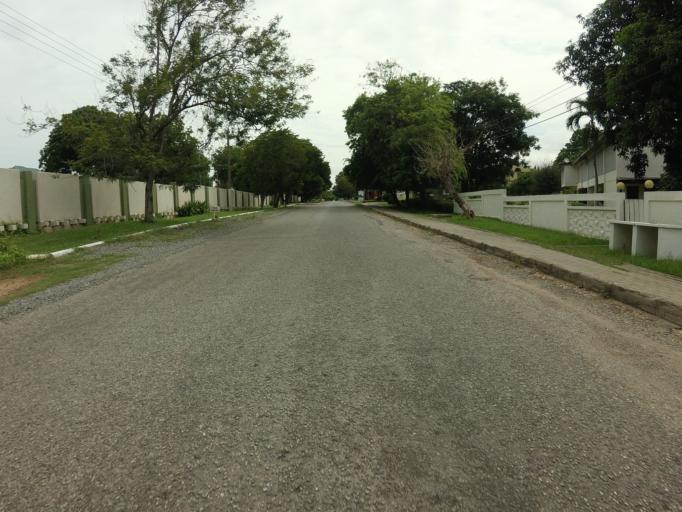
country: GH
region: Greater Accra
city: Accra
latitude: 5.6000
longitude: -0.1906
